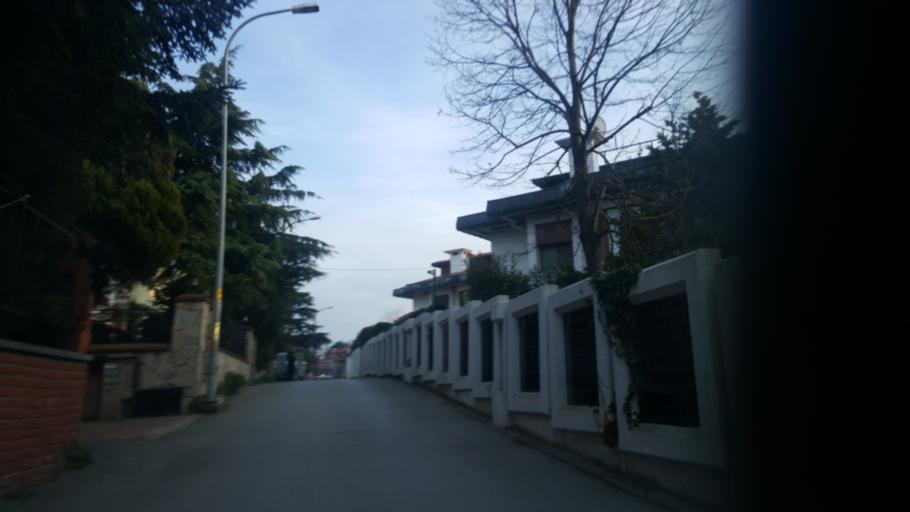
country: TR
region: Istanbul
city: Icmeler
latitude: 40.8180
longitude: 29.2718
